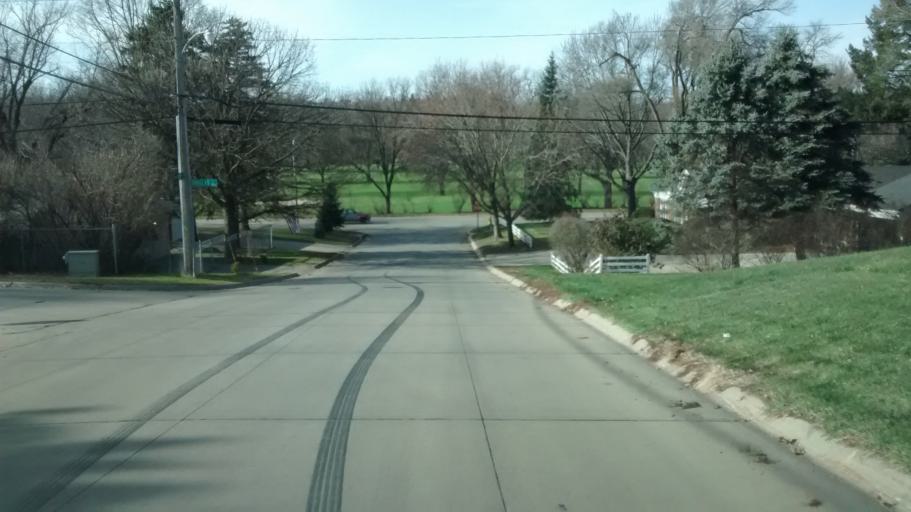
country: US
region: Iowa
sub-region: Woodbury County
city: Sioux City
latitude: 42.5376
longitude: -96.4072
